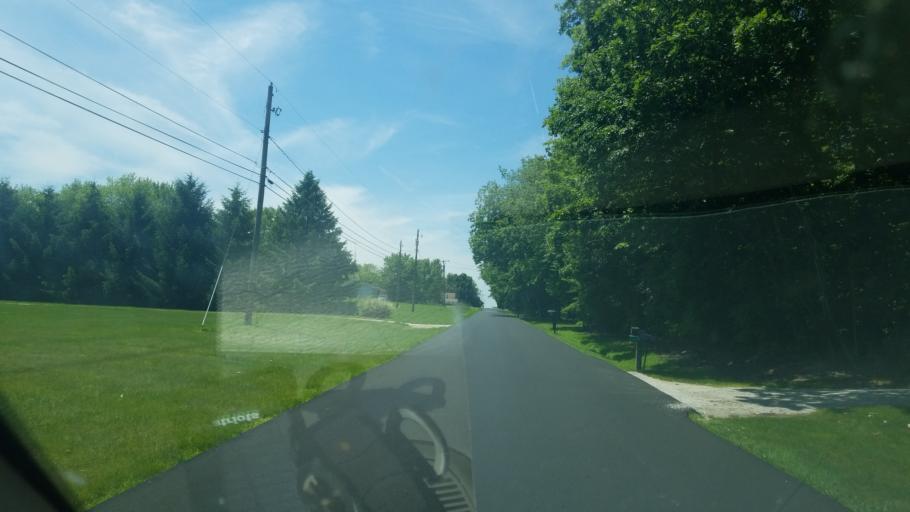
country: US
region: Ohio
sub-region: Stark County
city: Alliance
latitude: 40.8580
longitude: -81.1677
